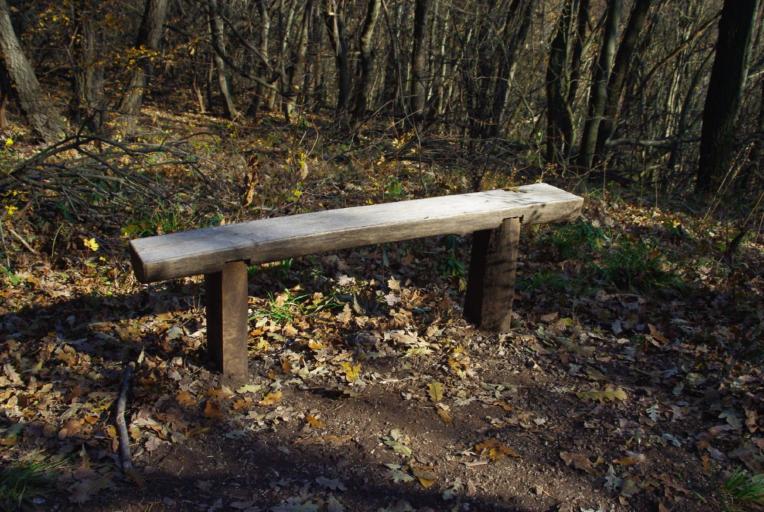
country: HU
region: Pest
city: Piliscsaba
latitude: 47.6452
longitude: 18.8343
